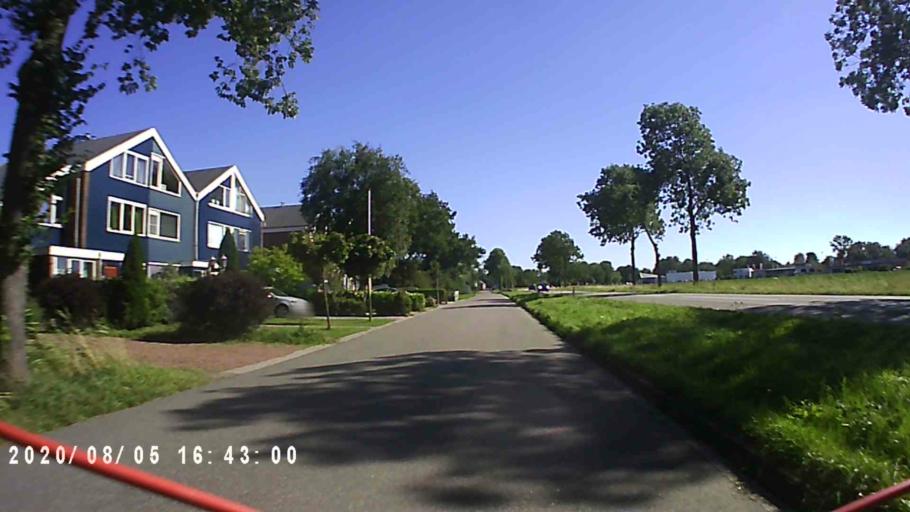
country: NL
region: Groningen
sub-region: Gemeente Winsum
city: Winsum
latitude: 53.3377
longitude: 6.5114
